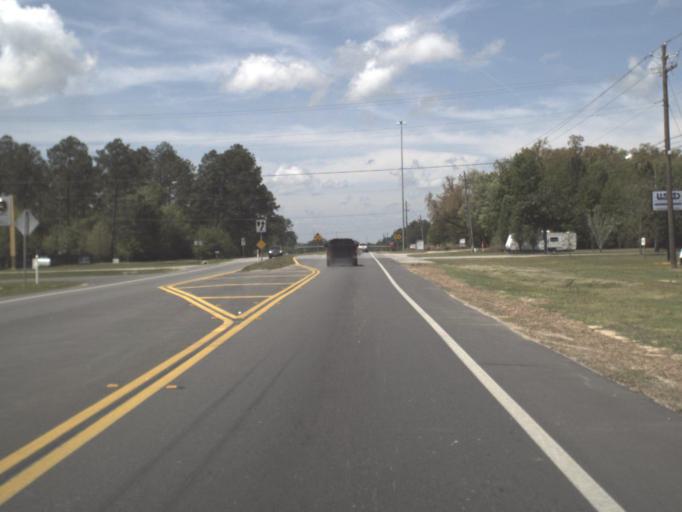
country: US
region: Florida
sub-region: Escambia County
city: Ensley
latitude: 30.5345
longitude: -87.3272
